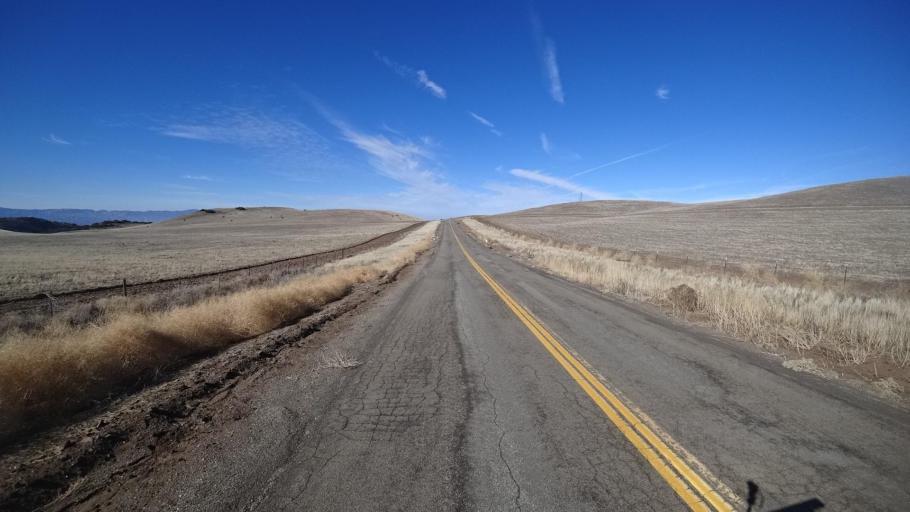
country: US
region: California
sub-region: Kern County
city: Maricopa
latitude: 34.9136
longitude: -119.3997
